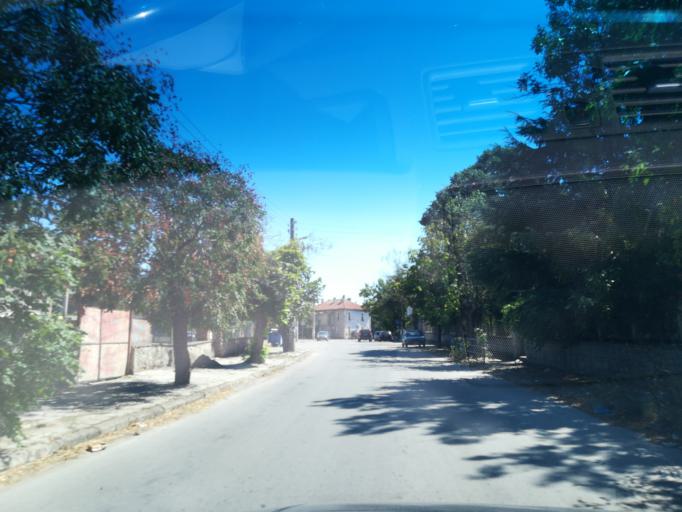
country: BG
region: Pazardzhik
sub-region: Obshtina Pazardzhik
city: Pazardzhik
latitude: 42.3332
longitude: 24.4013
